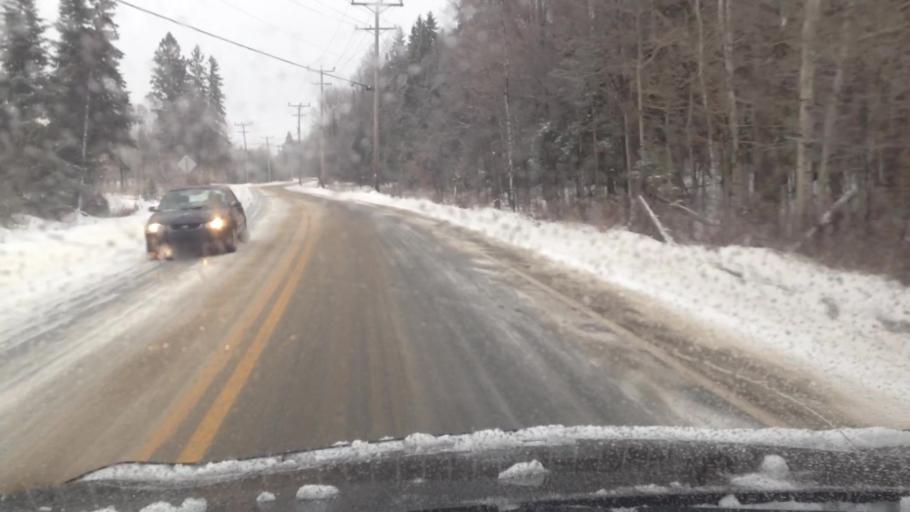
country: CA
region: Quebec
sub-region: Laurentides
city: Mont-Tremblant
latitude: 46.0081
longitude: -74.6157
